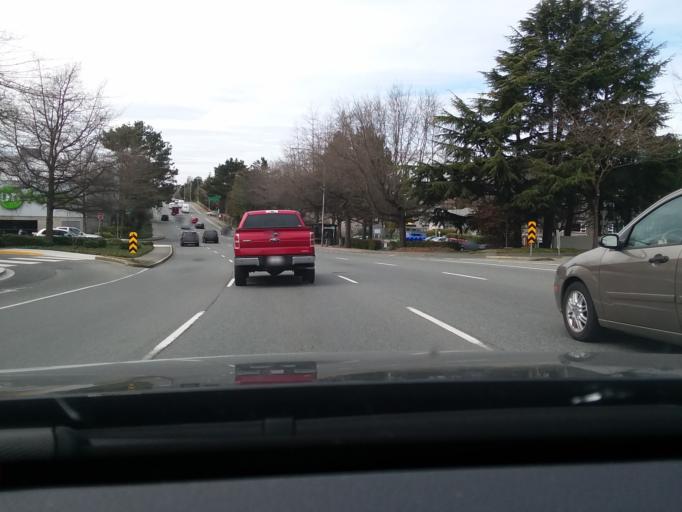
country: CA
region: British Columbia
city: Victoria
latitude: 48.4564
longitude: -123.3714
